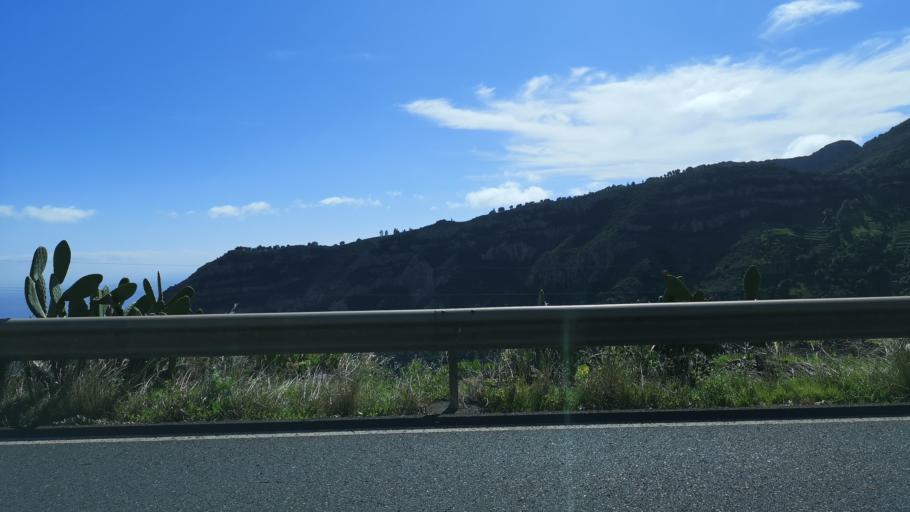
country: ES
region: Canary Islands
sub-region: Provincia de Santa Cruz de Tenerife
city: Alajero
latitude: 28.0936
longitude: -17.1944
